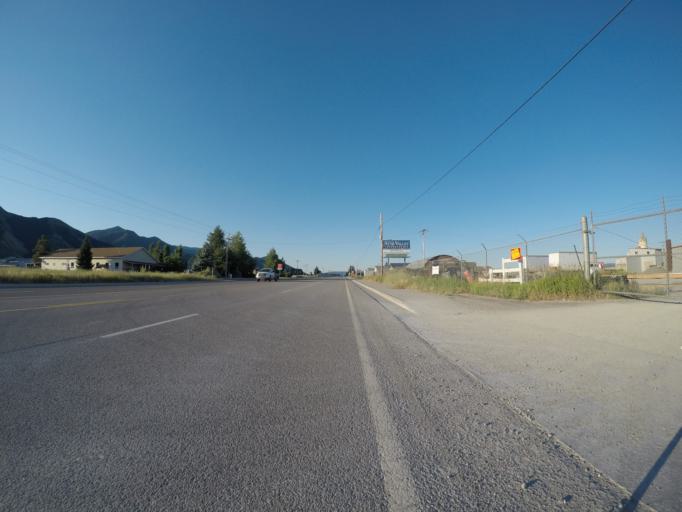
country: US
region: Wyoming
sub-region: Lincoln County
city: Afton
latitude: 42.7477
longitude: -110.9335
